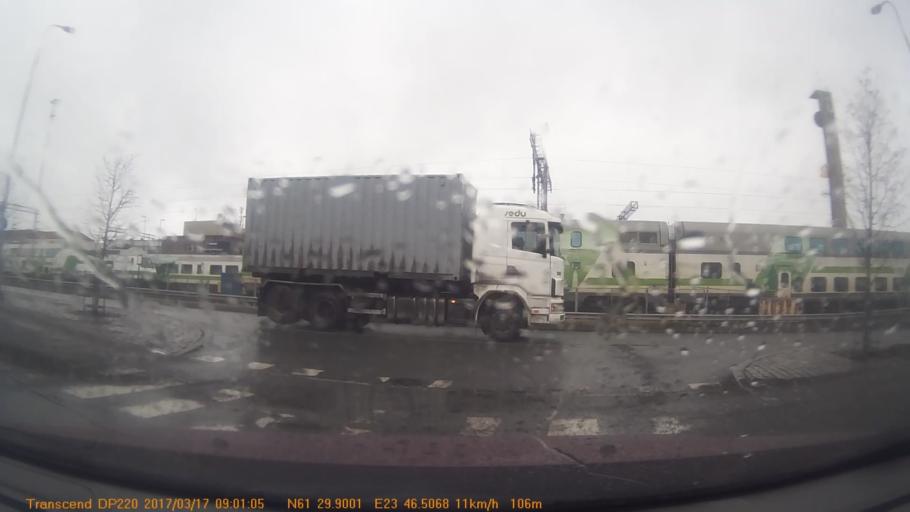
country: FI
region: Pirkanmaa
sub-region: Tampere
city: Tampere
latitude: 61.4985
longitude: 23.7754
